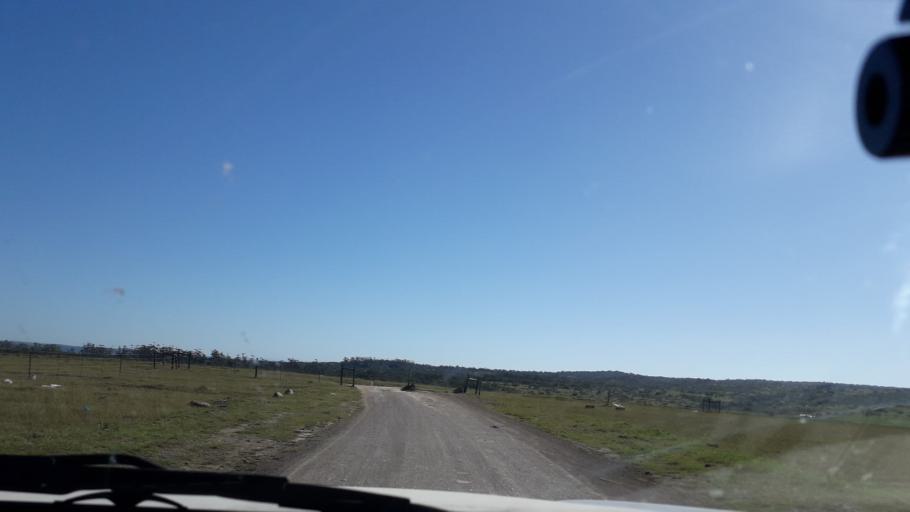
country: ZA
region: Eastern Cape
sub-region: Buffalo City Metropolitan Municipality
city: East London
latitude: -32.7975
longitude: 27.9519
